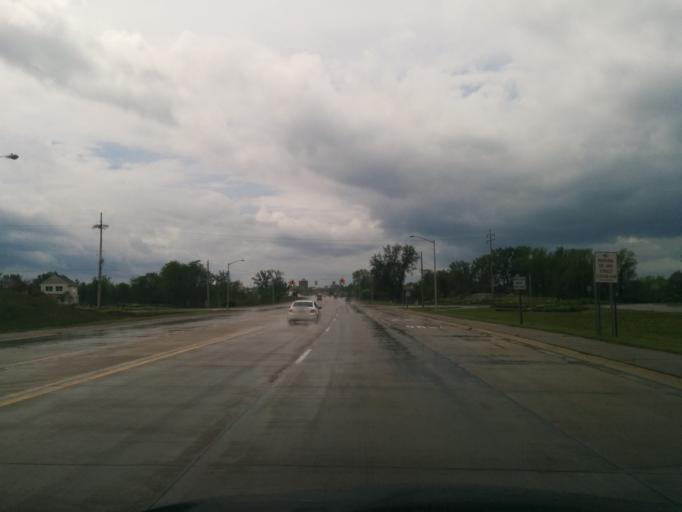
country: US
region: Michigan
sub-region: Berrien County
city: Benton Harbor
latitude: 42.1244
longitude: -86.4673
